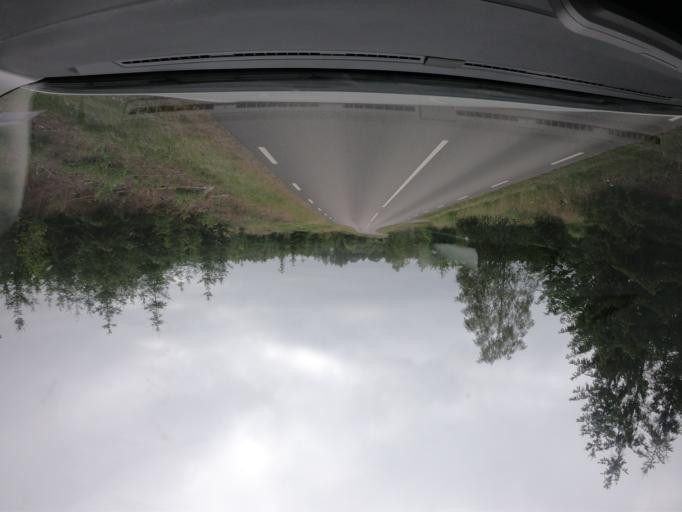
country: SE
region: Skane
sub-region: Perstorps Kommun
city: Perstorp
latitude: 56.0916
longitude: 13.4075
